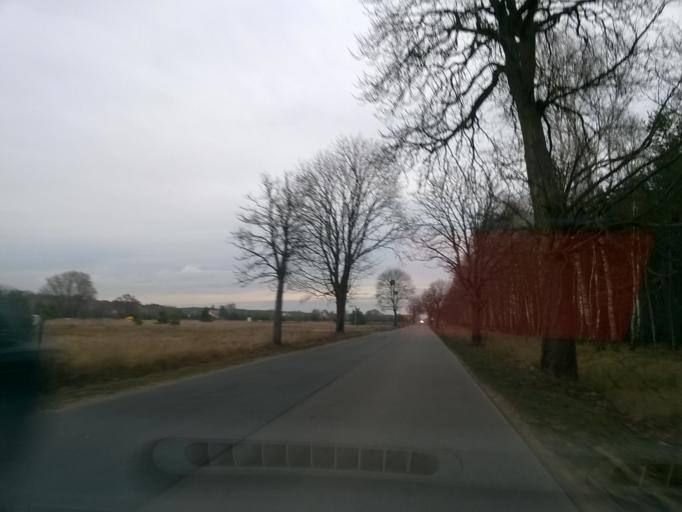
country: PL
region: Kujawsko-Pomorskie
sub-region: Powiat nakielski
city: Szubin
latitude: 53.0796
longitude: 17.7870
